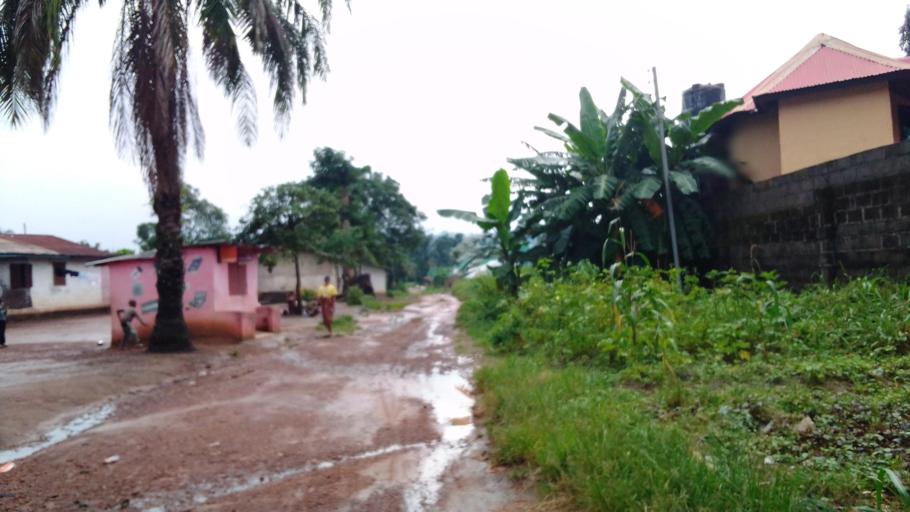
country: SL
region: Eastern Province
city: Kenema
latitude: 7.8542
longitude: -11.1971
